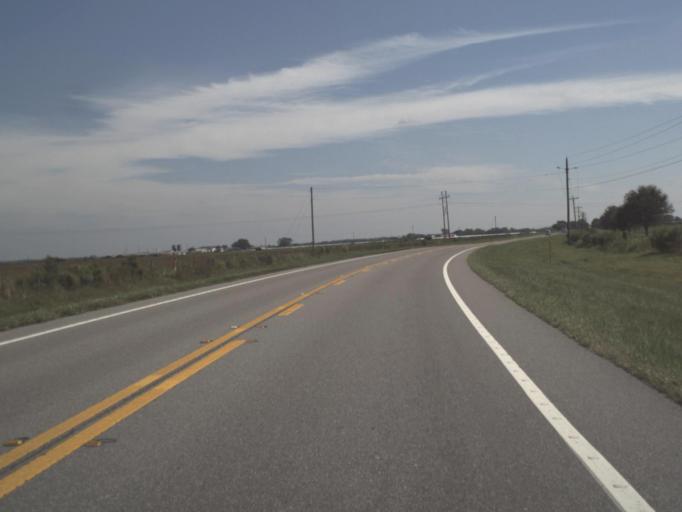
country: US
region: Florida
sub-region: Highlands County
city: Avon Park
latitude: 27.5865
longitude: -81.6018
